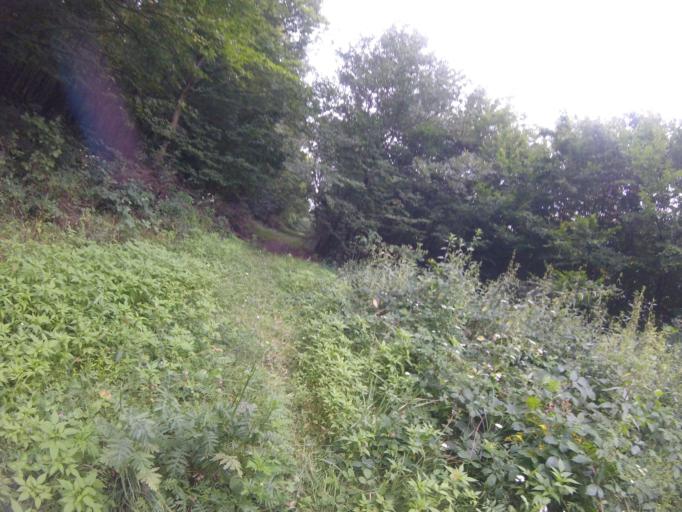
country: SK
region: Nitriansky
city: Sahy
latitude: 48.0298
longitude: 18.9794
